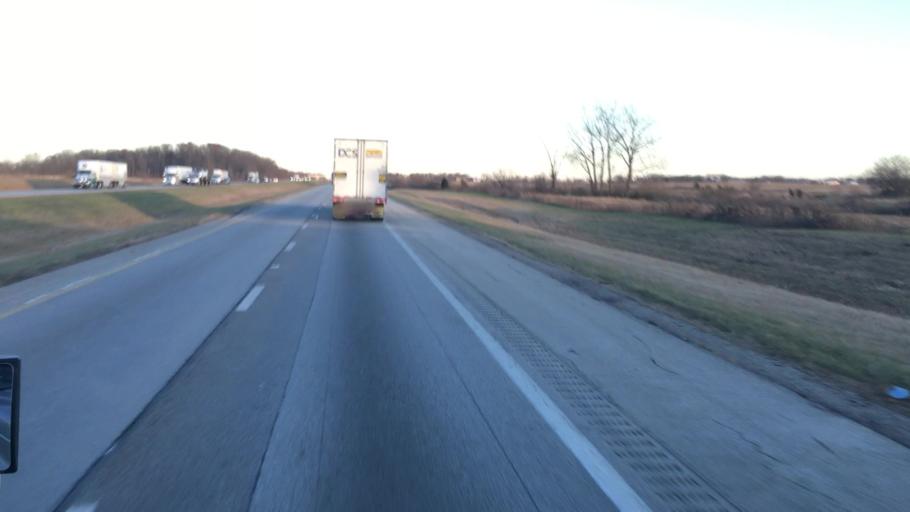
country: US
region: Ohio
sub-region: Preble County
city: Lewisburg
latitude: 39.8375
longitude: -84.5024
